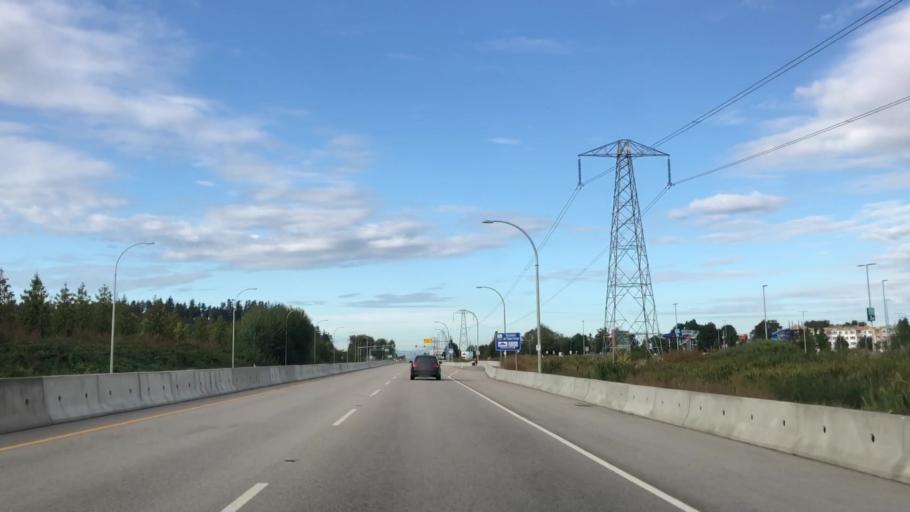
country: US
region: Washington
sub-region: Whatcom County
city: Point Roberts
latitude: 49.0347
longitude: -123.0859
